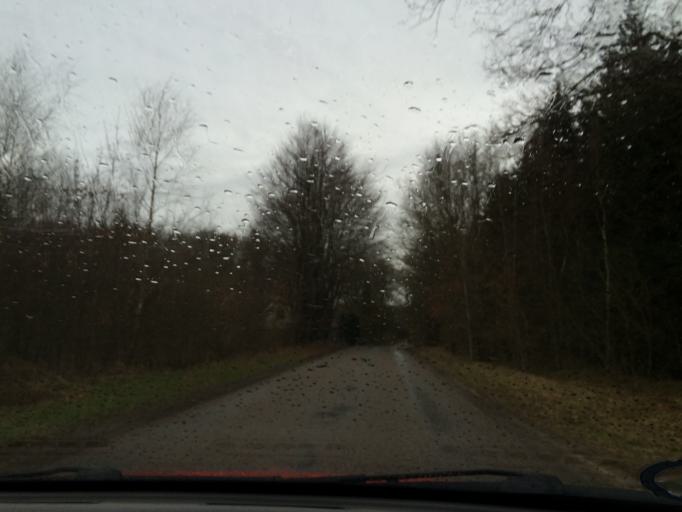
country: DK
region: Central Jutland
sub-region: Silkeborg Kommune
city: Virklund
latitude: 56.0288
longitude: 9.4607
